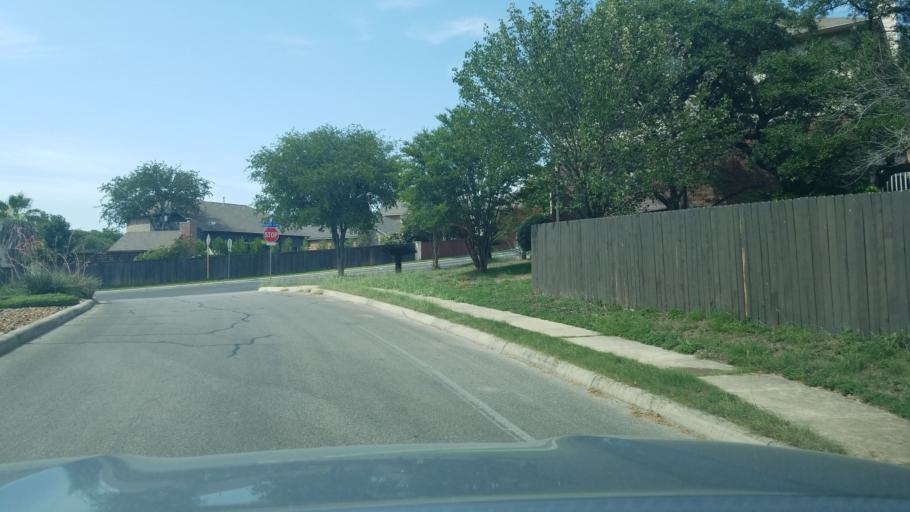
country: US
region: Texas
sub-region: Bexar County
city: Hollywood Park
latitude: 29.6315
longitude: -98.4891
